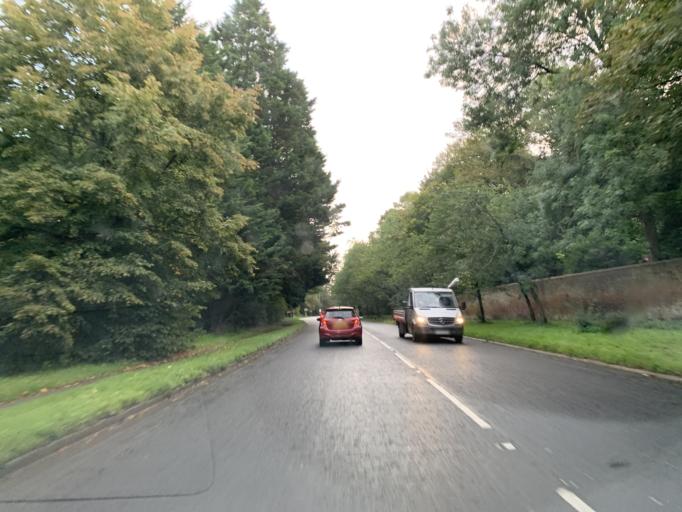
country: GB
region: England
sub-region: Hampshire
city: Romsey
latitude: 50.9861
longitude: -1.4977
